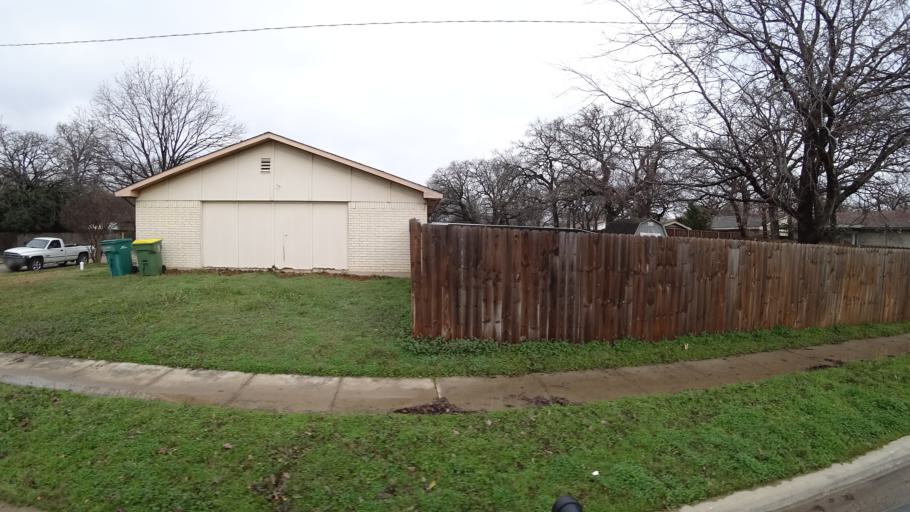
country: US
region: Texas
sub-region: Denton County
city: Lewisville
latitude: 33.0314
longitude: -97.0212
